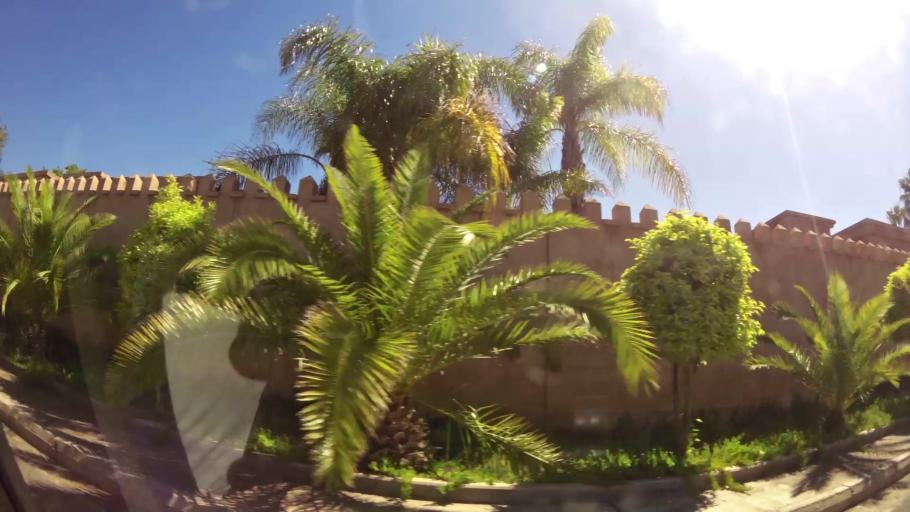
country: MA
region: Marrakech-Tensift-Al Haouz
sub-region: Marrakech
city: Marrakesh
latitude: 31.6584
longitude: -7.9612
